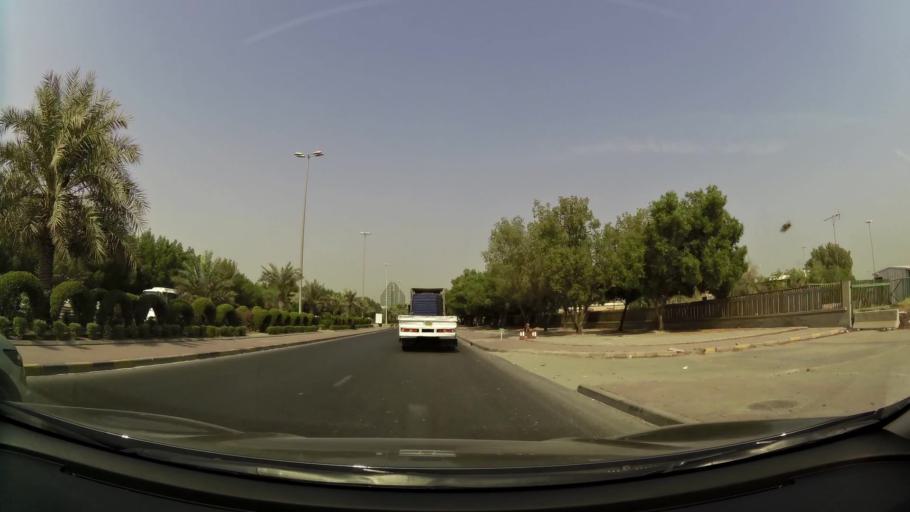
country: KW
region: Al Asimah
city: Ar Rabiyah
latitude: 29.3233
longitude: 47.9227
